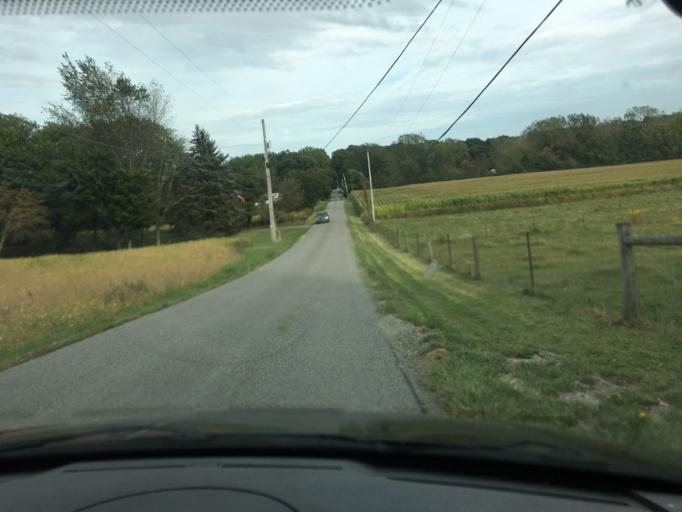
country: US
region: Ohio
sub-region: Logan County
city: Bellefontaine
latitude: 40.3187
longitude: -83.7832
